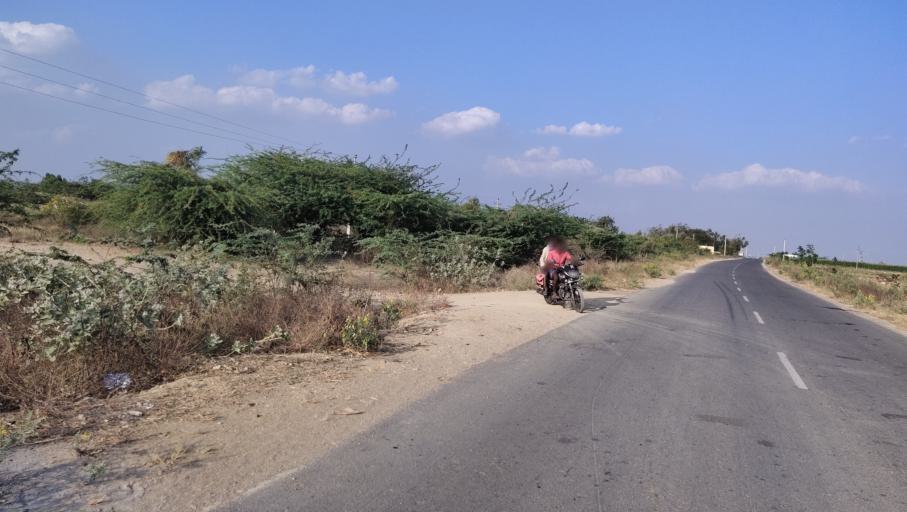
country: IN
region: Andhra Pradesh
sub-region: Anantapur
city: Tadpatri
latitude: 14.9434
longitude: 77.8727
